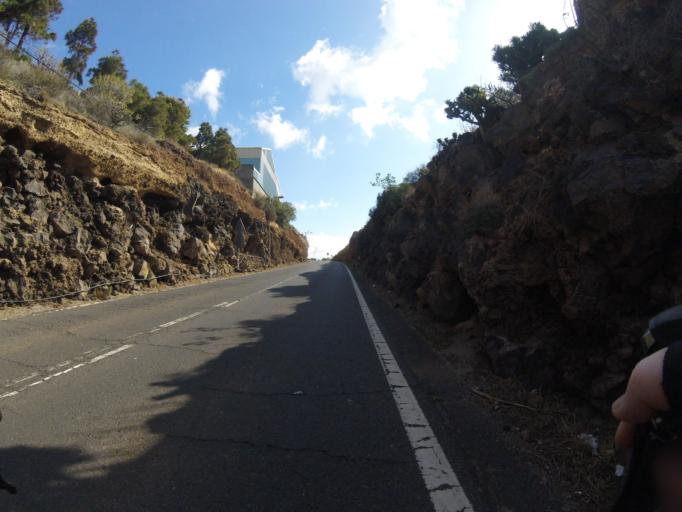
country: ES
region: Canary Islands
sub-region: Provincia de Santa Cruz de Tenerife
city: La Laguna
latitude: 28.4167
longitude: -16.3213
